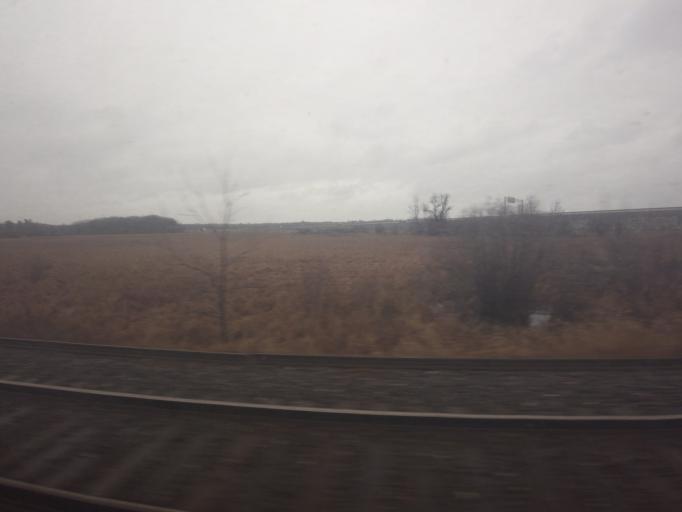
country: CA
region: Ontario
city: Kingston
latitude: 44.2802
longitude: -76.4684
